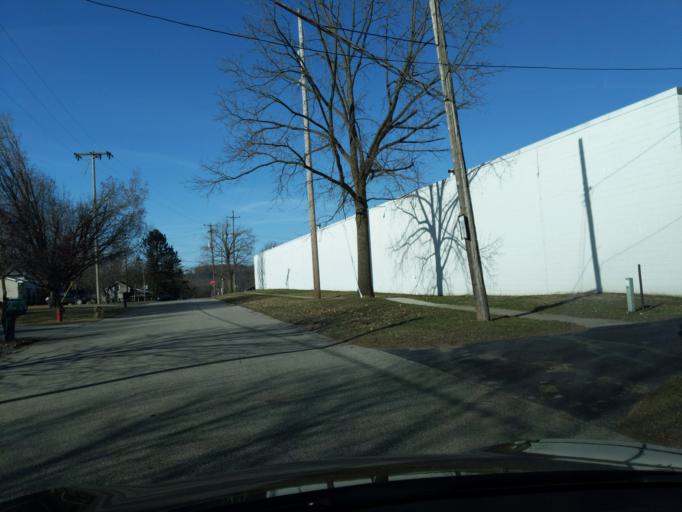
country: US
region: Michigan
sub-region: Ionia County
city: Saranac
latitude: 42.9304
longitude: -85.2035
